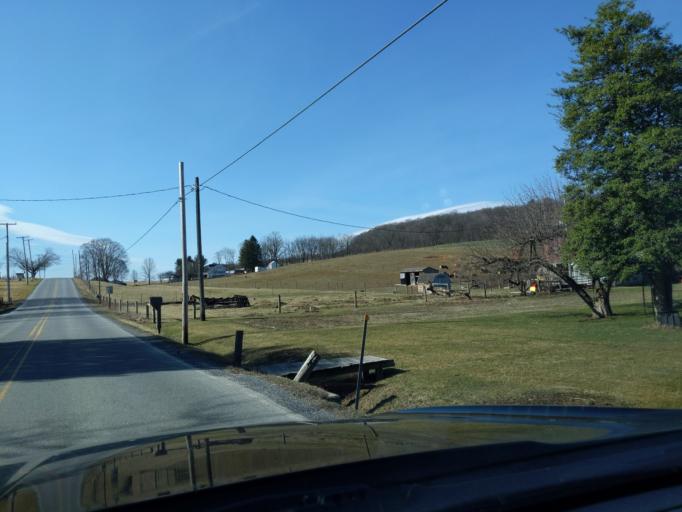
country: US
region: Pennsylvania
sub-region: Blair County
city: Williamsburg
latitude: 40.3737
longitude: -78.2366
